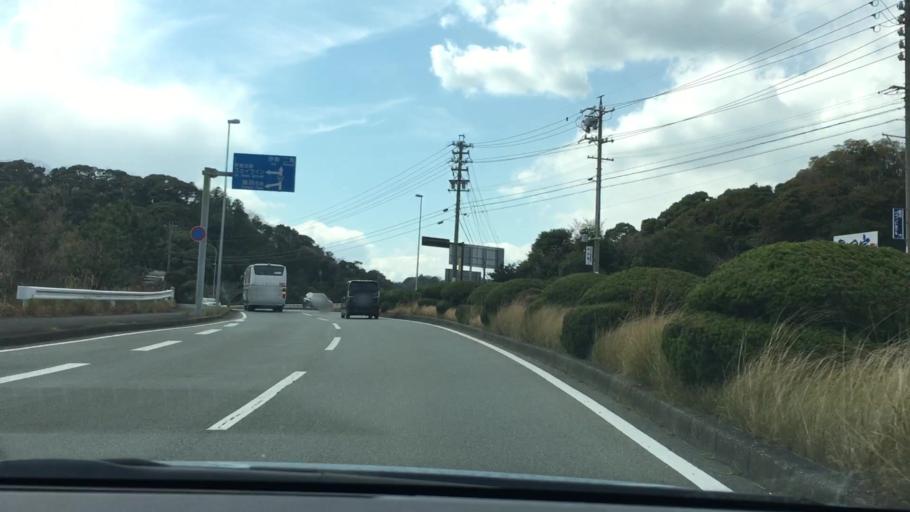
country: JP
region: Mie
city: Toba
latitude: 34.4882
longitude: 136.8406
